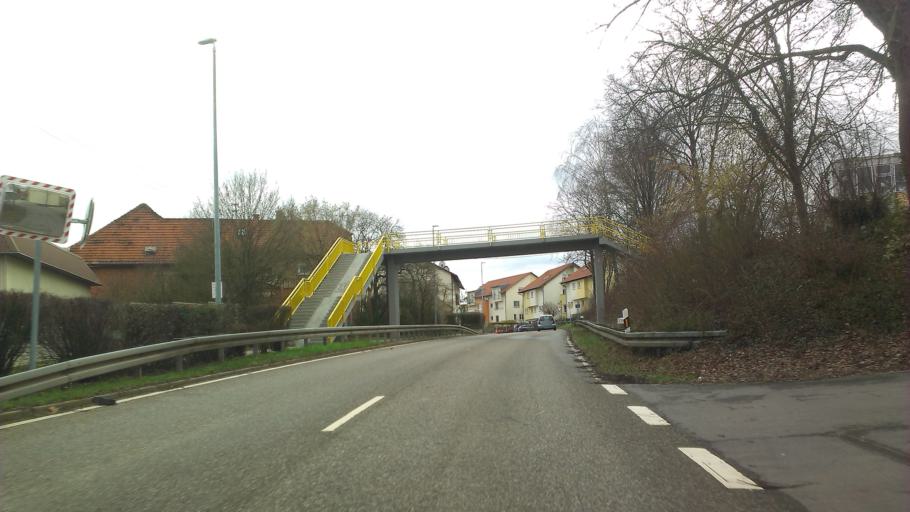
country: DE
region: Baden-Wuerttemberg
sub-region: Regierungsbezirk Stuttgart
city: Sersheim
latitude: 48.9622
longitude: 9.0094
